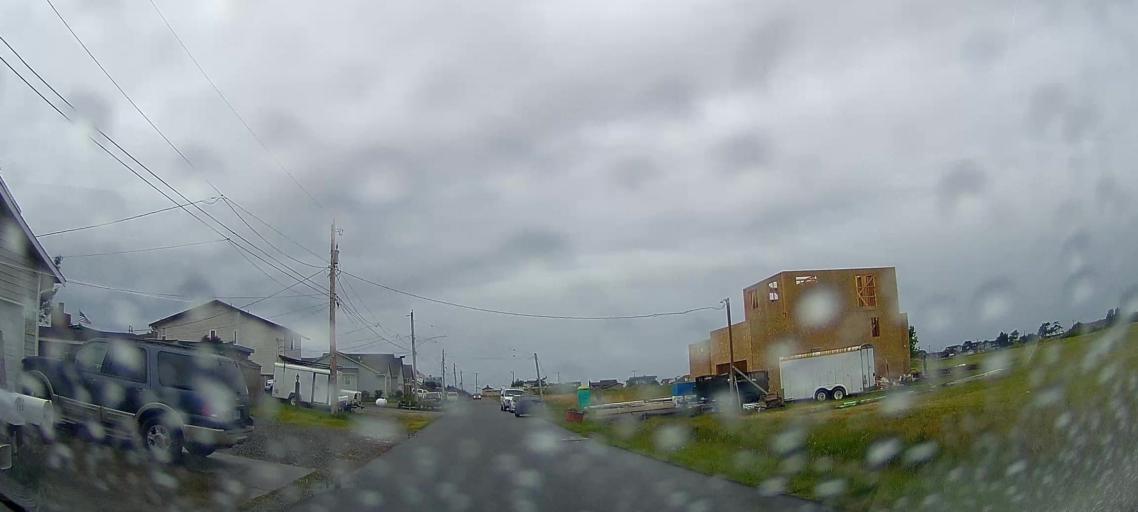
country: US
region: Washington
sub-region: Whatcom County
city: Marietta
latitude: 48.7915
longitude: -122.7055
